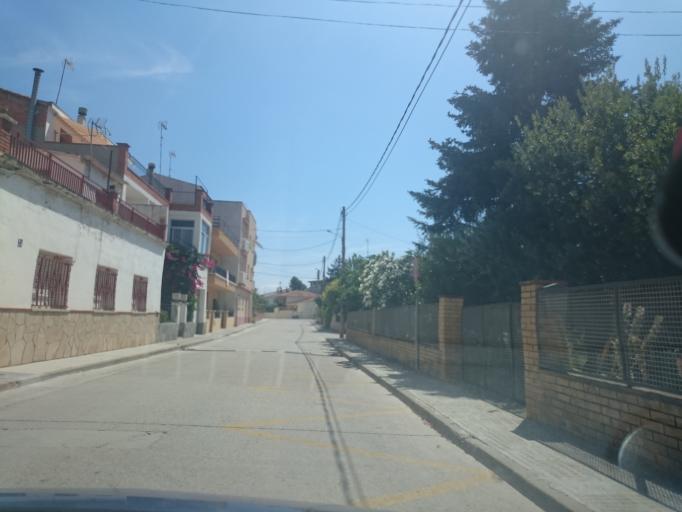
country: ES
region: Catalonia
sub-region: Provincia de Barcelona
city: Sant Pere de Riudebitlles
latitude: 41.4612
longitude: 1.6652
